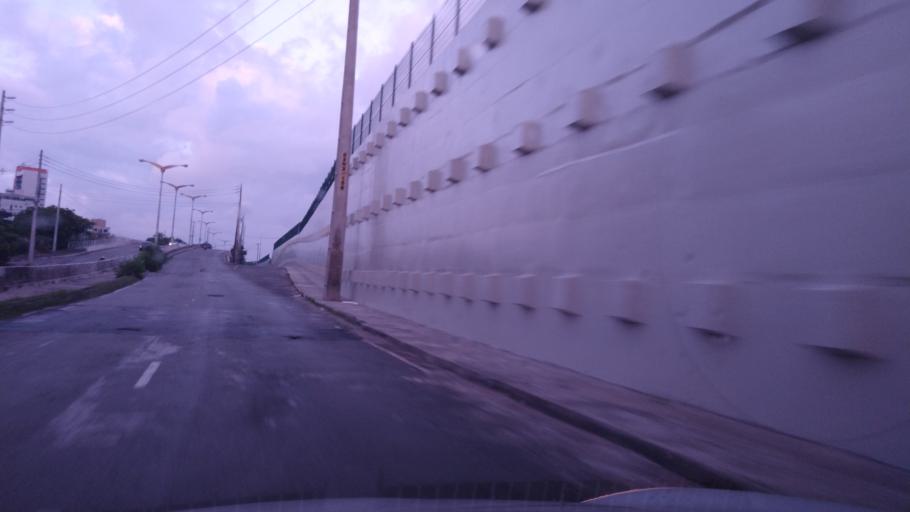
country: BR
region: Ceara
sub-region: Fortaleza
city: Fortaleza
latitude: -3.7470
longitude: -38.4920
